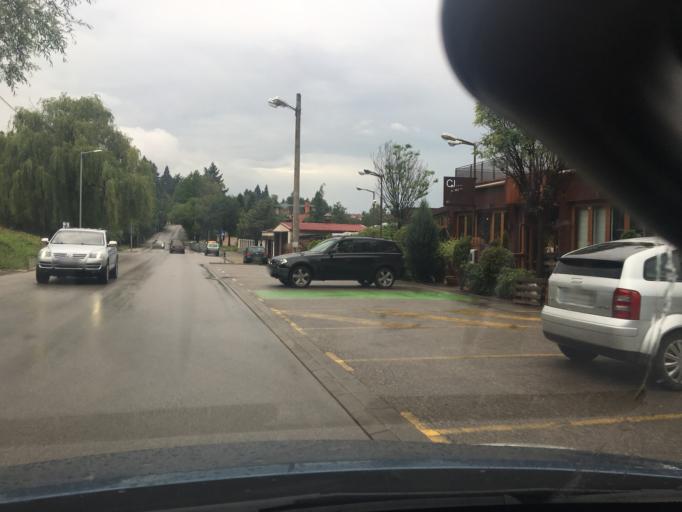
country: BG
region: Sofia-Capital
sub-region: Stolichna Obshtina
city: Sofia
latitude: 42.6429
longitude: 23.2830
